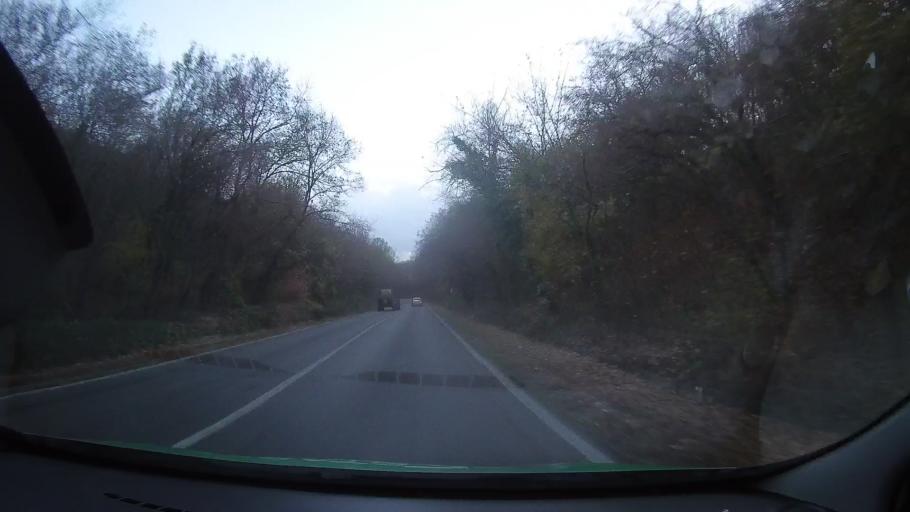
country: RO
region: Constanta
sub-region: Comuna Baneasa
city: Baneasa
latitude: 44.0937
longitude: 27.6535
